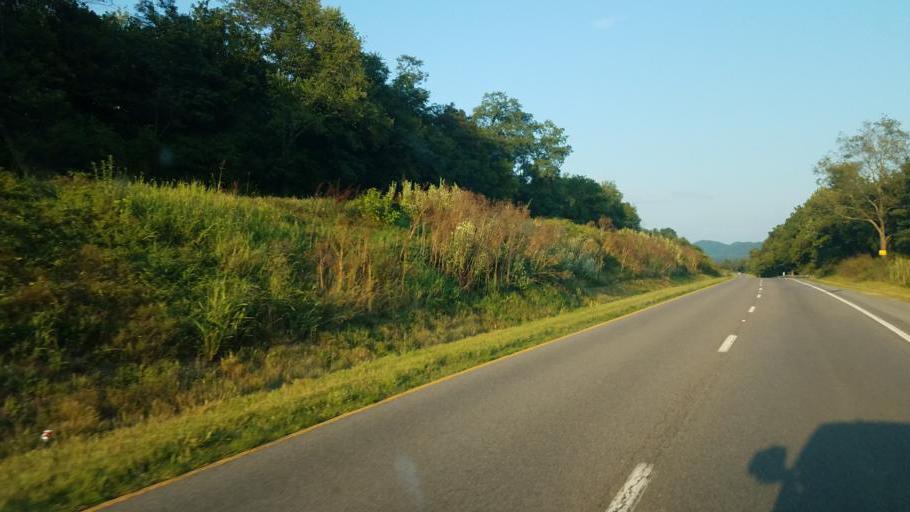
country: US
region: Virginia
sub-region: Scott County
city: Gate City
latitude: 36.6362
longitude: -82.6491
